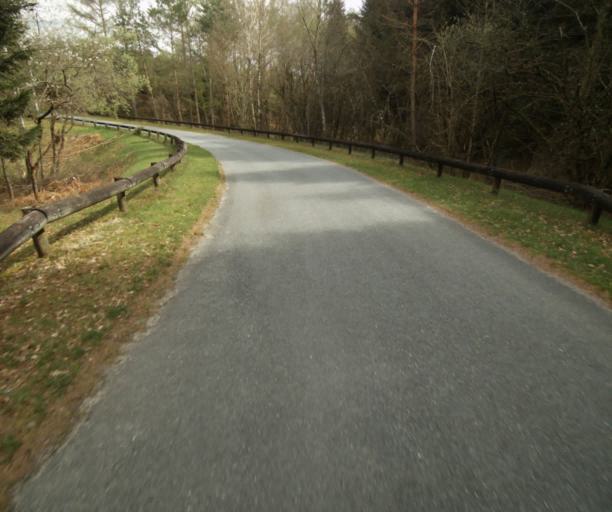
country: FR
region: Limousin
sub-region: Departement de la Correze
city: Correze
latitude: 45.2889
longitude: 1.9560
